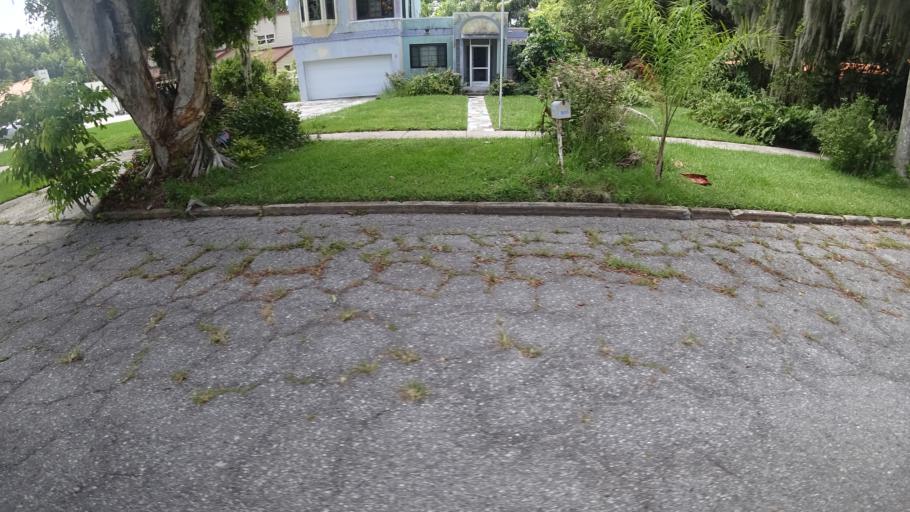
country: US
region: Florida
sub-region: Manatee County
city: Whitfield
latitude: 27.4051
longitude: -82.5711
